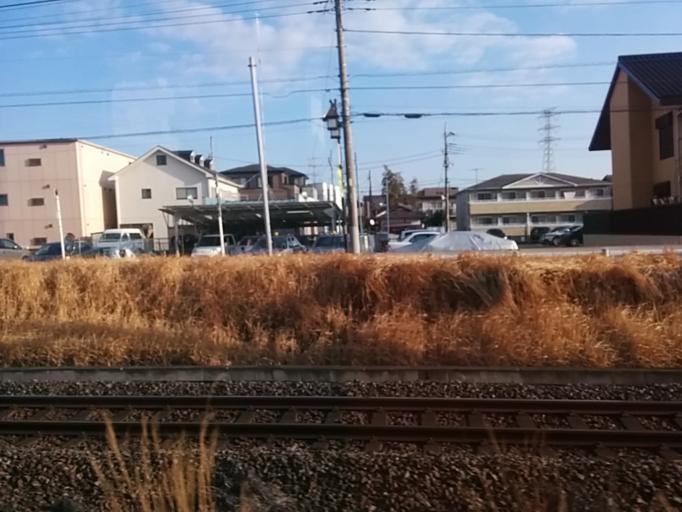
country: JP
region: Saitama
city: Oi
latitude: 35.8392
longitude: 139.5495
